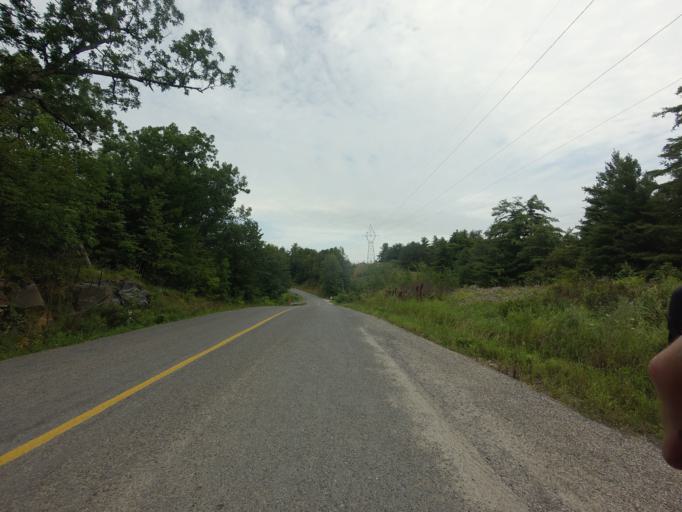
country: CA
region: Ontario
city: Kingston
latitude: 44.6566
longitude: -76.6544
